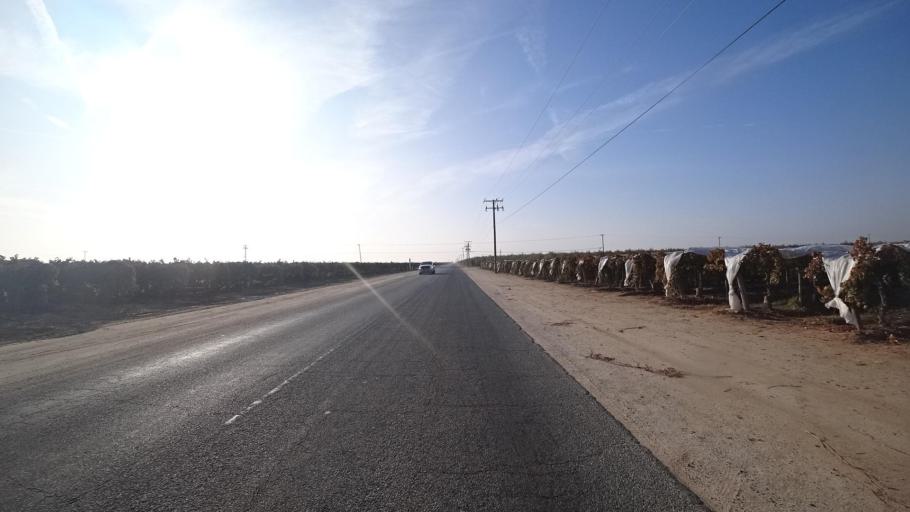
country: US
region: California
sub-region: Kern County
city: McFarland
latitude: 35.6759
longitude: -119.2048
